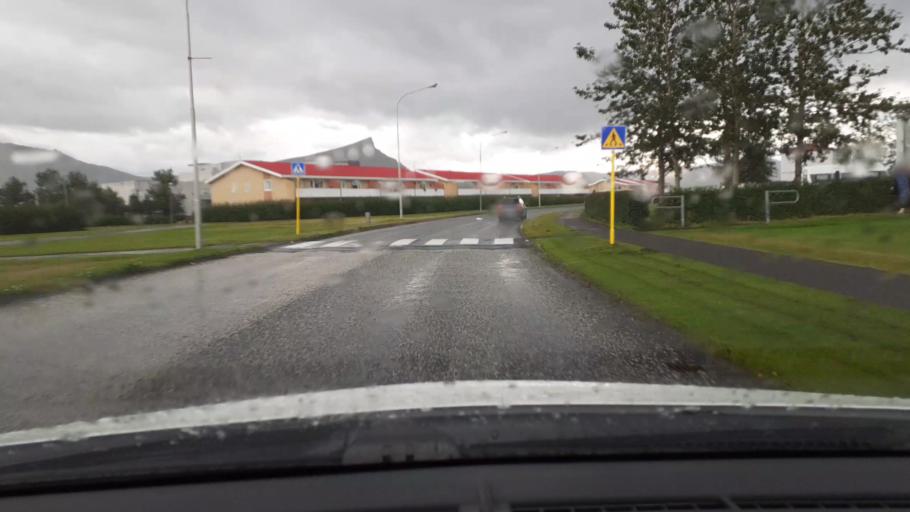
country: IS
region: West
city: Akranes
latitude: 64.3212
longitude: -22.0563
